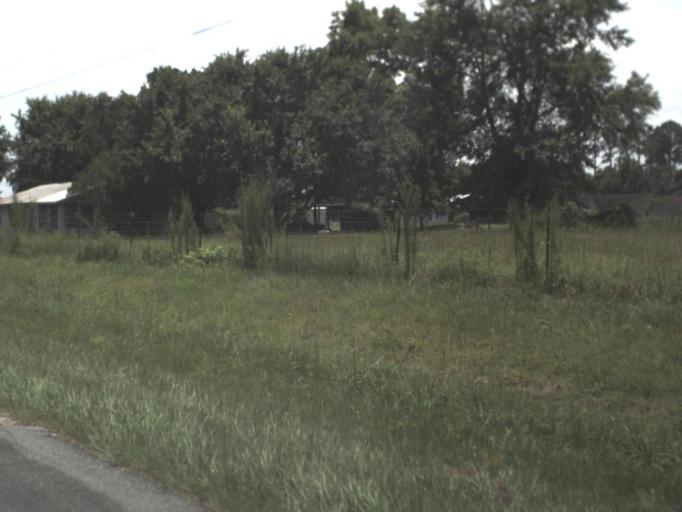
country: US
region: Florida
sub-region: Bradford County
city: Starke
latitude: 30.0368
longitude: -82.1636
